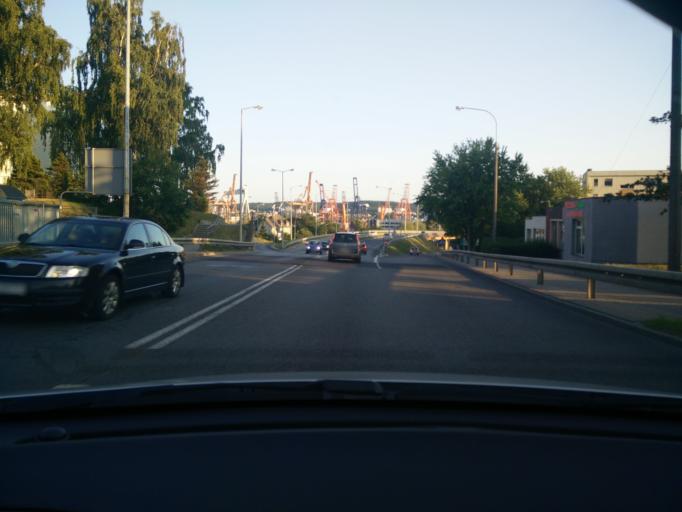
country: PL
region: Pomeranian Voivodeship
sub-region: Gdynia
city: Pogorze
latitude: 54.5533
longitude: 18.5075
